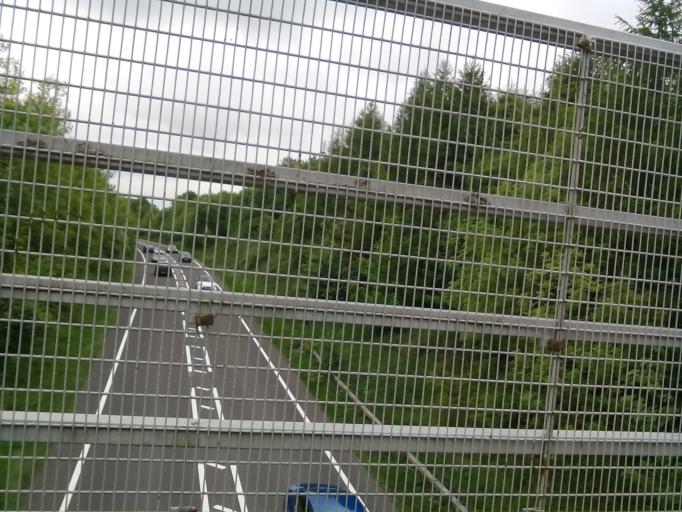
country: GB
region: England
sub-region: District of Rutland
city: South Luffenham
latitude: 52.5394
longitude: -0.5903
